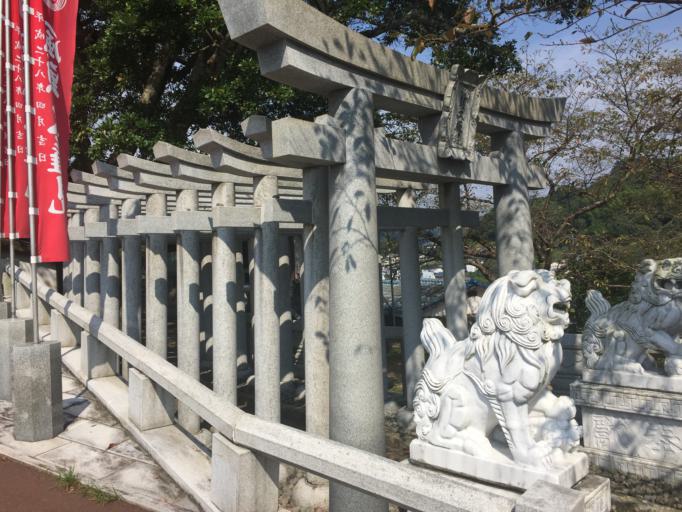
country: JP
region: Nagasaki
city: Nagasaki-shi
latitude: 32.7454
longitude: 129.8863
